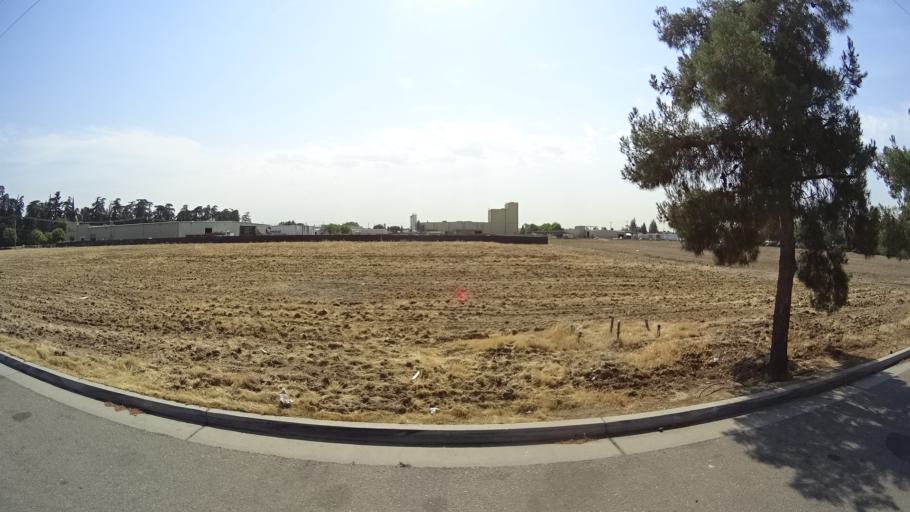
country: US
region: California
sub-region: Fresno County
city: West Park
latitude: 36.7415
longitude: -119.8267
